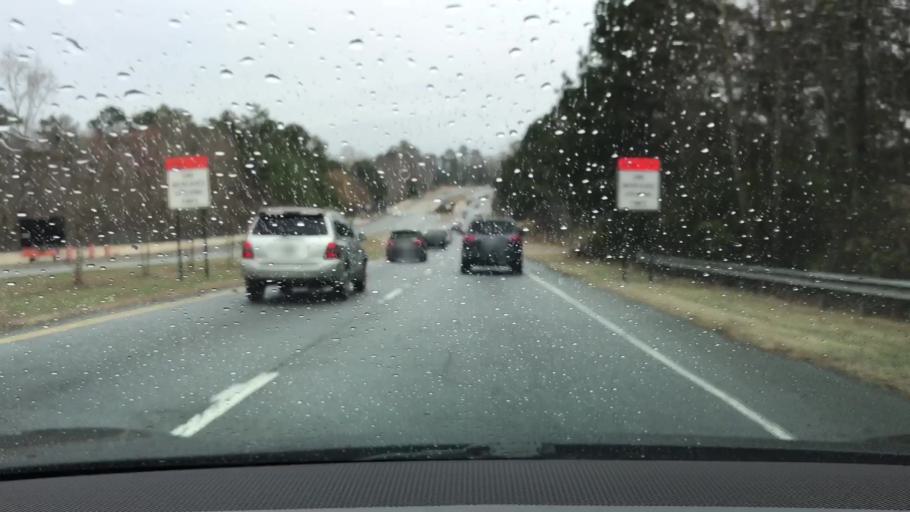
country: US
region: Georgia
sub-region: Gwinnett County
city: Suwanee
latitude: 34.0407
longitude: -84.0776
